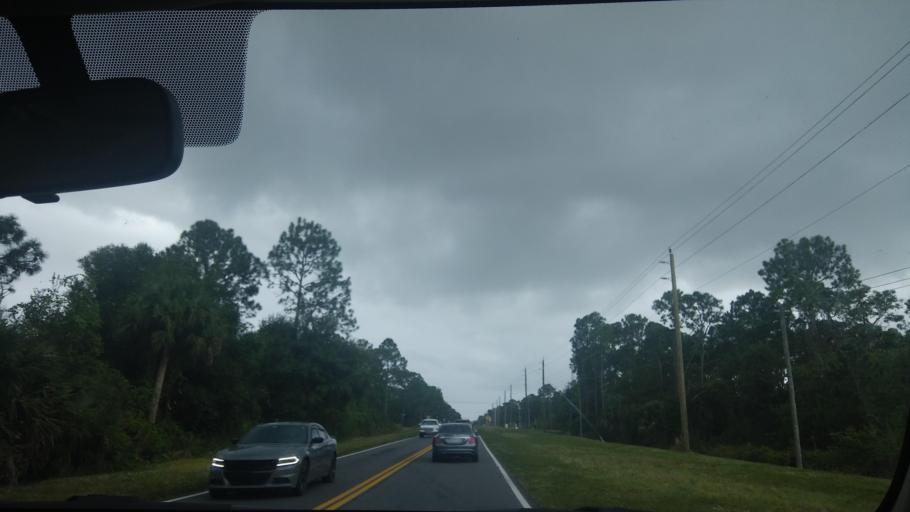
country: US
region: Florida
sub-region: Brevard County
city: Grant-Valkaria
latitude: 27.9709
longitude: -80.6226
